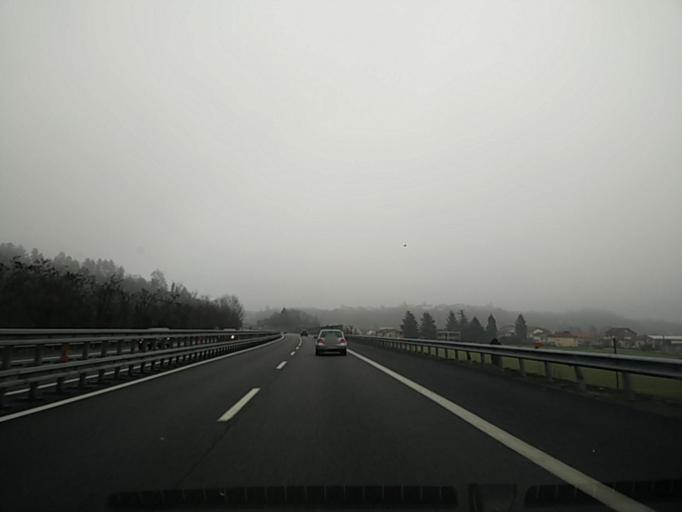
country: IT
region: Piedmont
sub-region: Provincia di Asti
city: Azzano d'Asti
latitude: 44.9086
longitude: 8.2764
